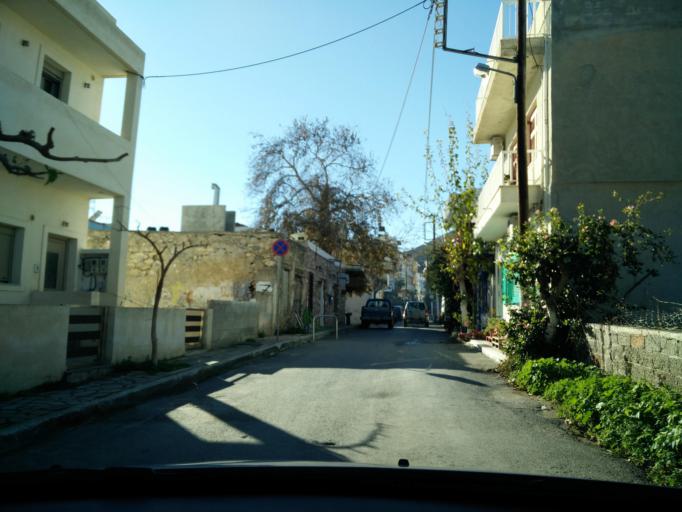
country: GR
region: Crete
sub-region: Nomos Lasithiou
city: Gra Liyia
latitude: 35.0042
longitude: 25.5857
